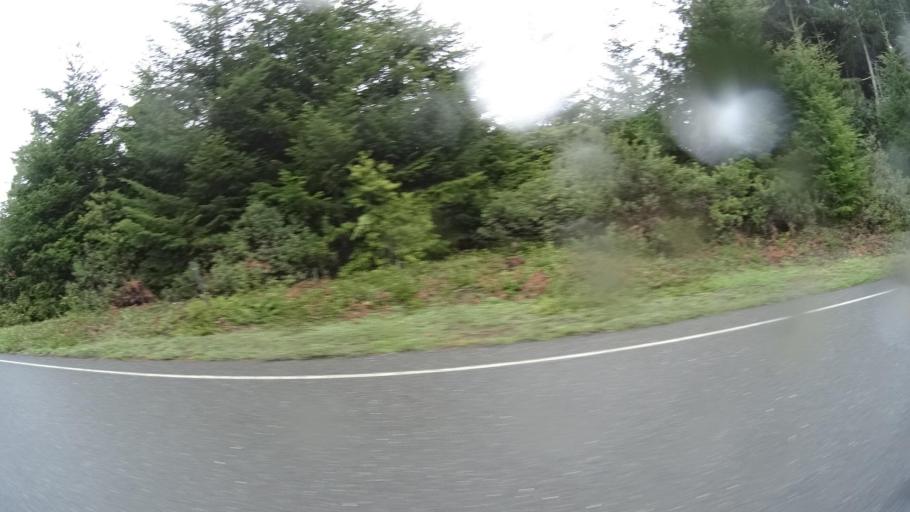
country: US
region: California
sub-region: Humboldt County
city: Willow Creek
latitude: 41.1669
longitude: -123.8154
